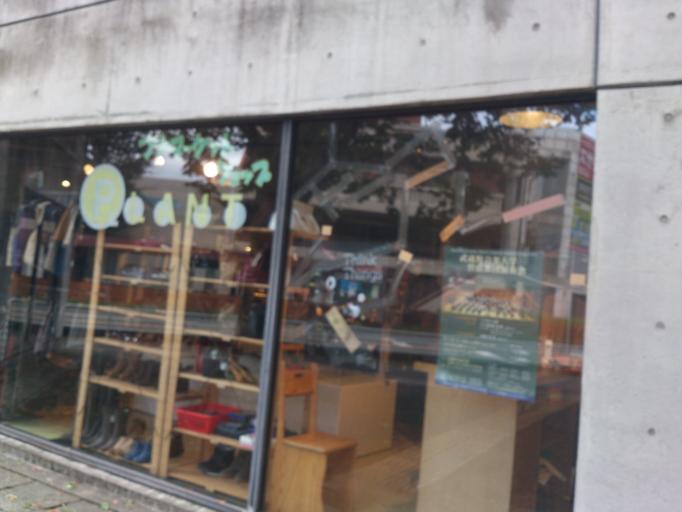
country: JP
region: Yamaguchi
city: Yamaguchi-shi
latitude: 34.1775
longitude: 131.4751
